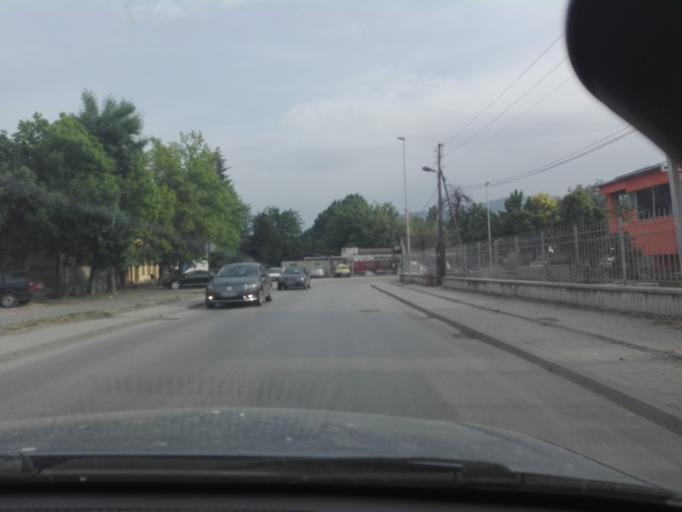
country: MK
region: Bitola
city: Bitola
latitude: 41.0202
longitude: 21.3423
